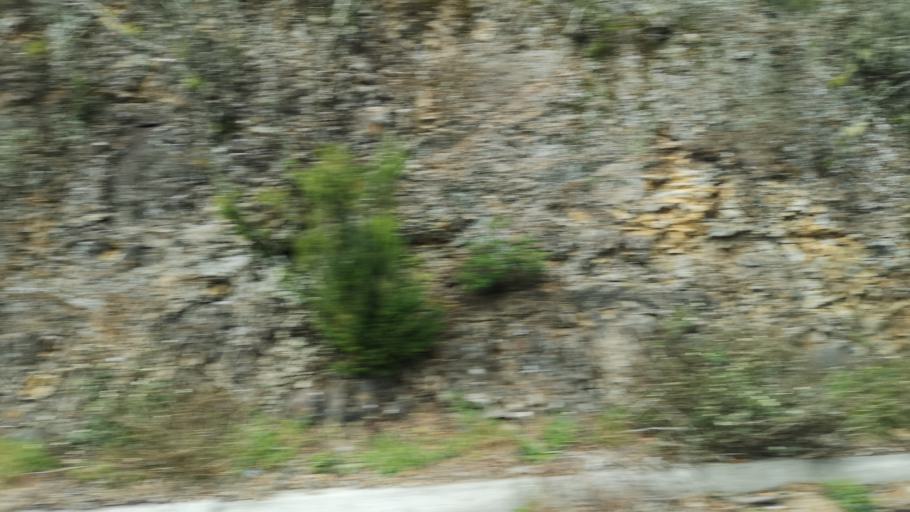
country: ES
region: Canary Islands
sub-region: Provincia de Santa Cruz de Tenerife
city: Vallehermosa
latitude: 28.1287
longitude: -17.2700
